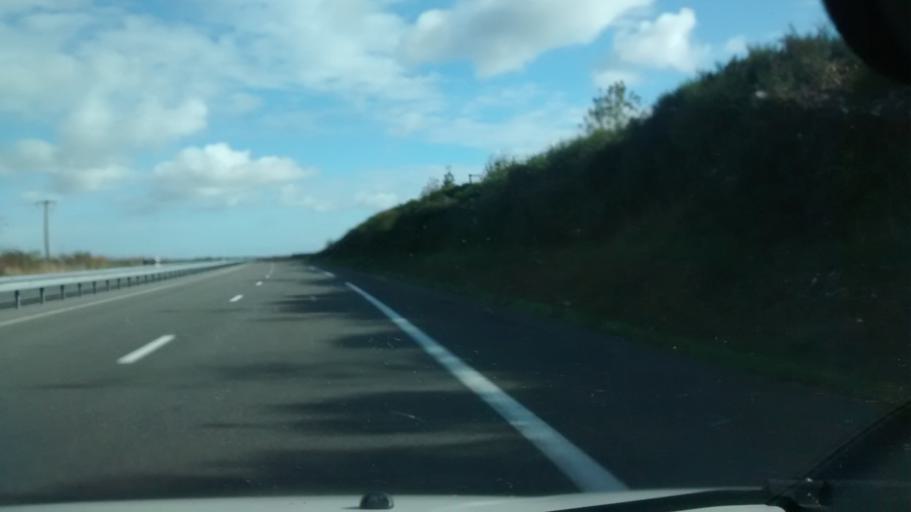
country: FR
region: Pays de la Loire
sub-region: Departement de Maine-et-Loire
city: Combree
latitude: 47.7291
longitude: -1.0899
